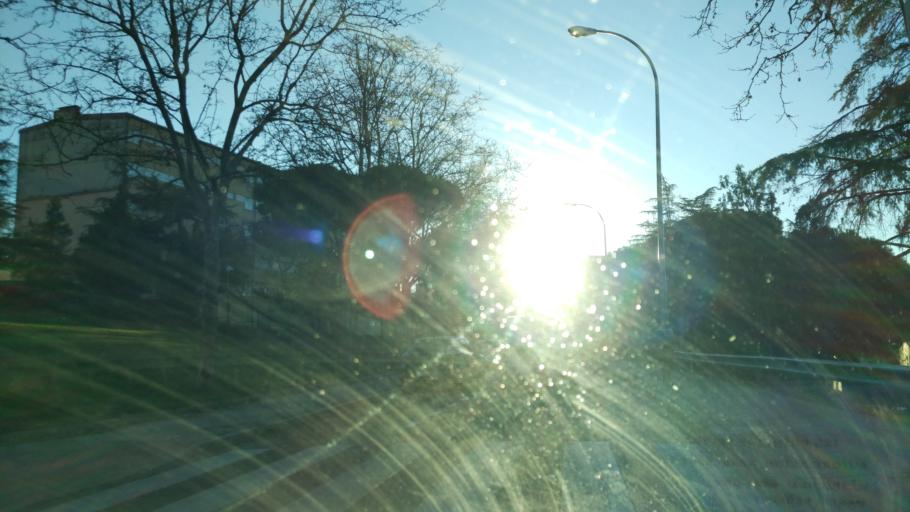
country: ES
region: Madrid
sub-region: Provincia de Madrid
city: Las Tablas
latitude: 40.4911
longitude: -3.6950
